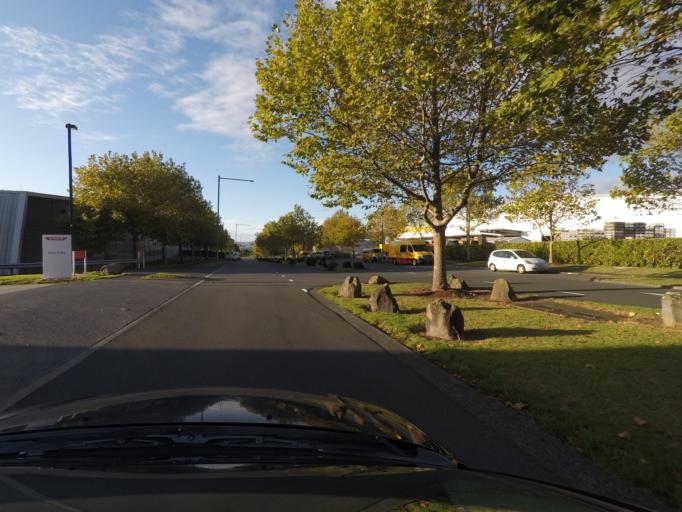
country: NZ
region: Auckland
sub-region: Auckland
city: Manukau City
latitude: -36.9405
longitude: 174.8752
